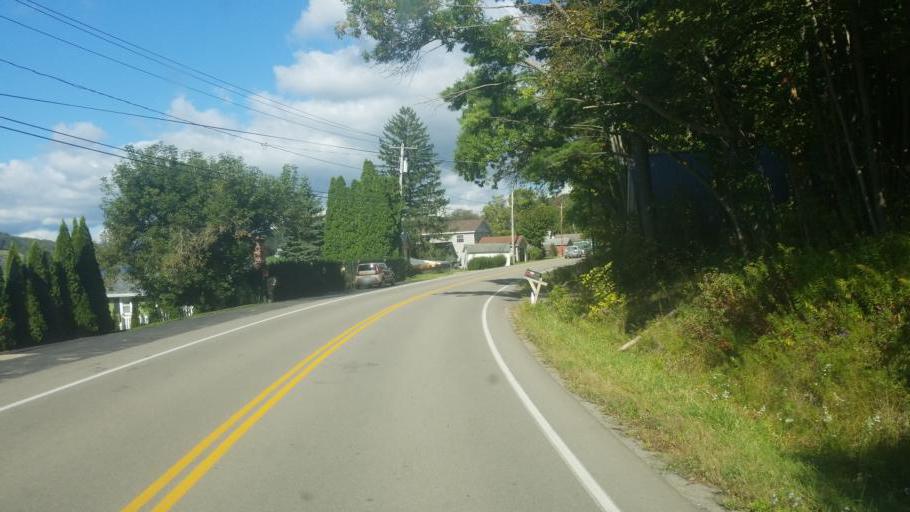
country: US
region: New York
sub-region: Allegany County
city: Cuba
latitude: 42.2495
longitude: -78.2757
